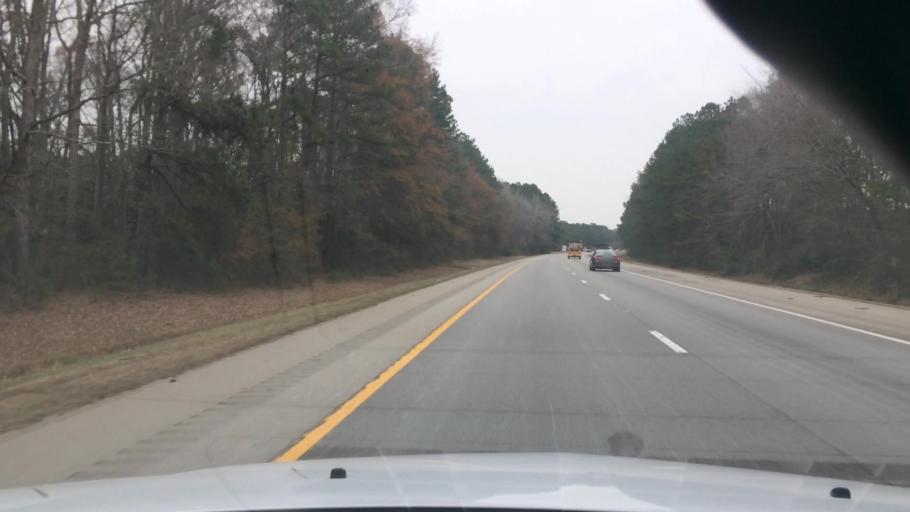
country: US
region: North Carolina
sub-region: Wilson County
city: Wilson
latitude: 35.7789
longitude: -78.0020
